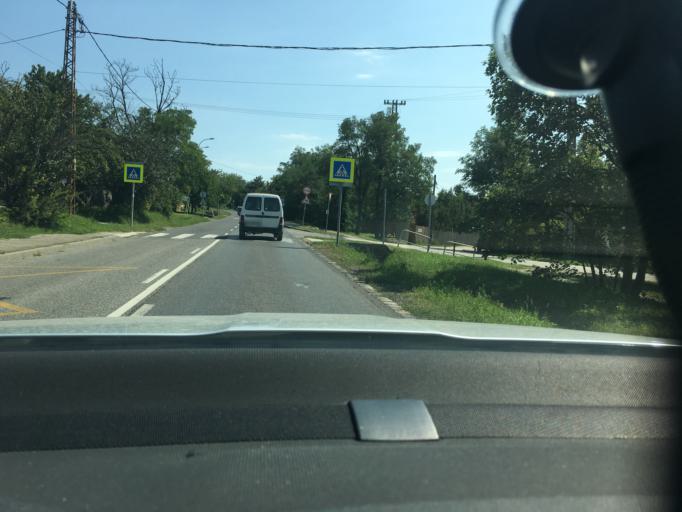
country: HU
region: Pest
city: Ecser
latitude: 47.4655
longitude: 19.3083
